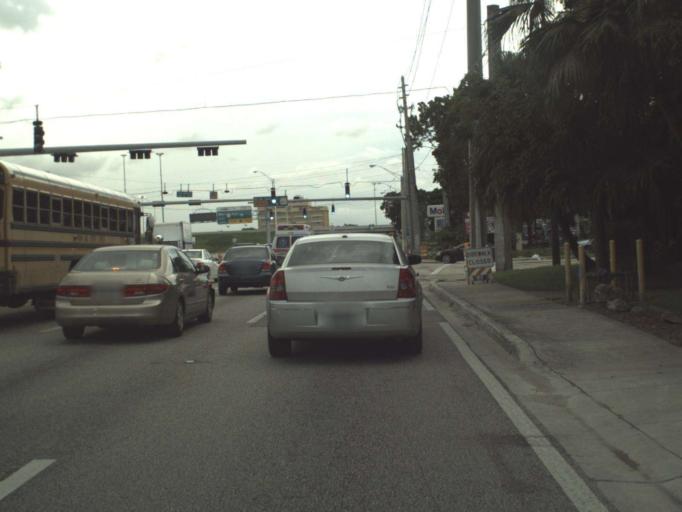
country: US
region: Florida
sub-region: Miami-Dade County
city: Flagami
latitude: 25.7762
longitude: -80.3123
